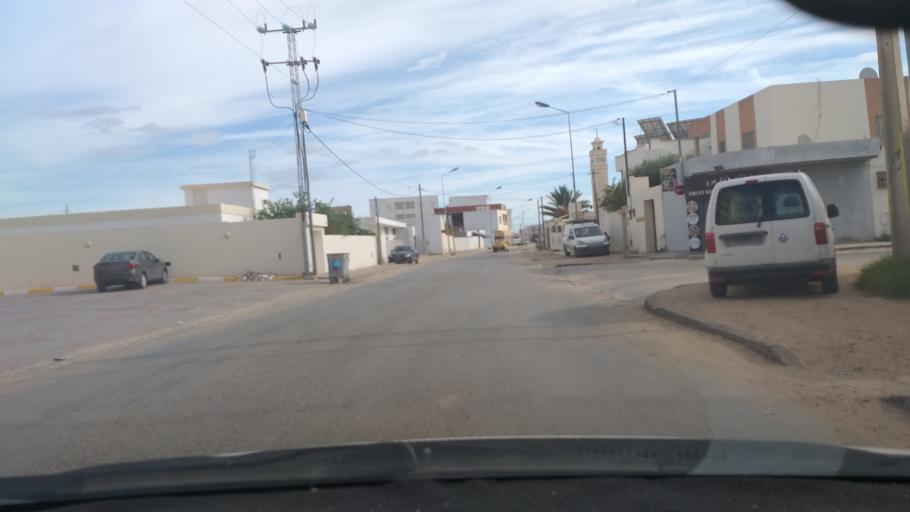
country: TN
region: Safaqis
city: Al Qarmadah
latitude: 34.7971
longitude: 10.7994
